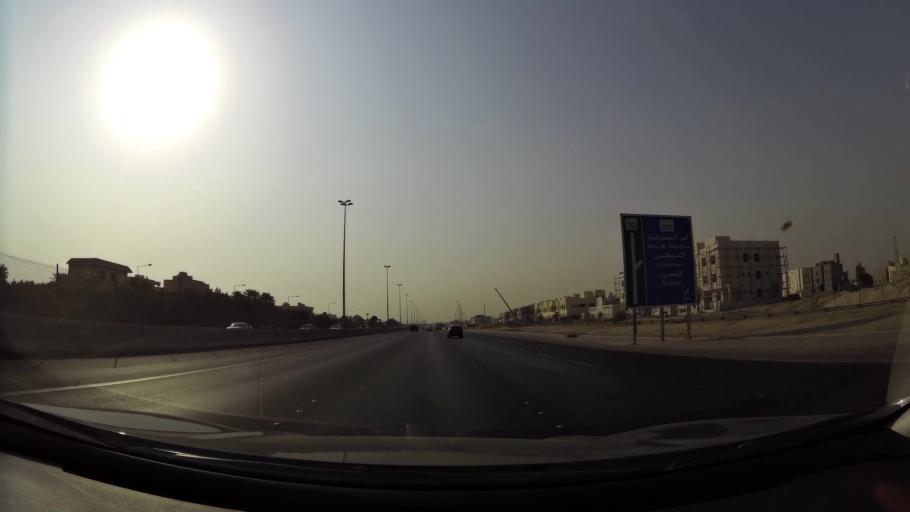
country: KW
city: Al Funaytis
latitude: 29.2259
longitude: 48.0990
